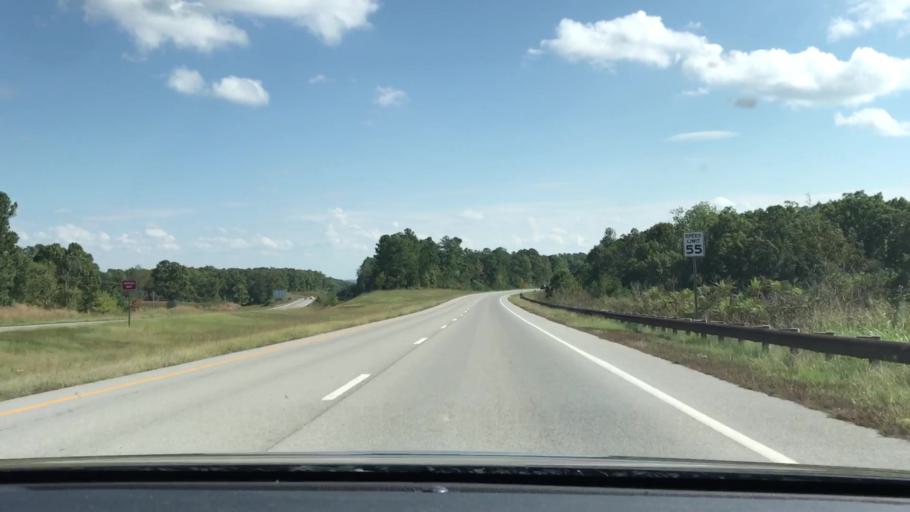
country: US
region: Kentucky
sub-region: Trigg County
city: Cadiz
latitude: 36.7812
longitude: -88.0513
